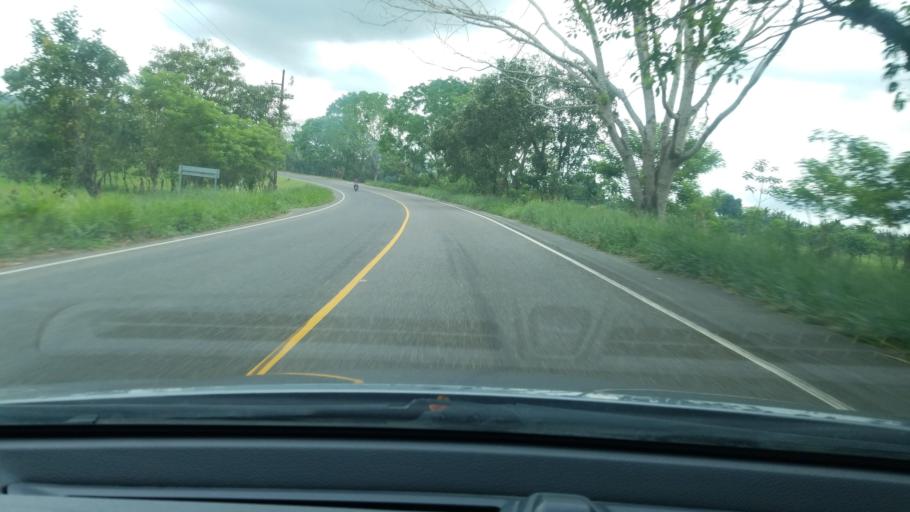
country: HN
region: Cortes
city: Potrerillos
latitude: 15.5963
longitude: -88.3193
